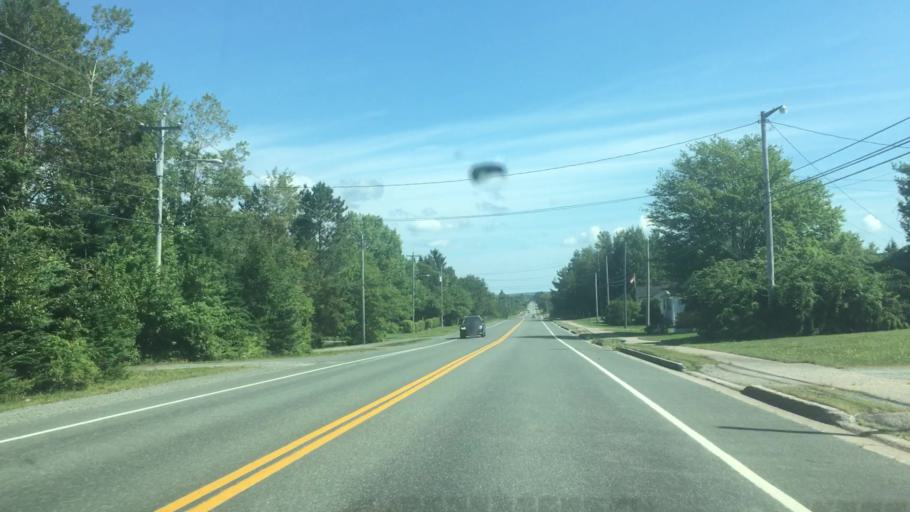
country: CA
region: Nova Scotia
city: Sydney
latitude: 46.0521
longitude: -60.3188
